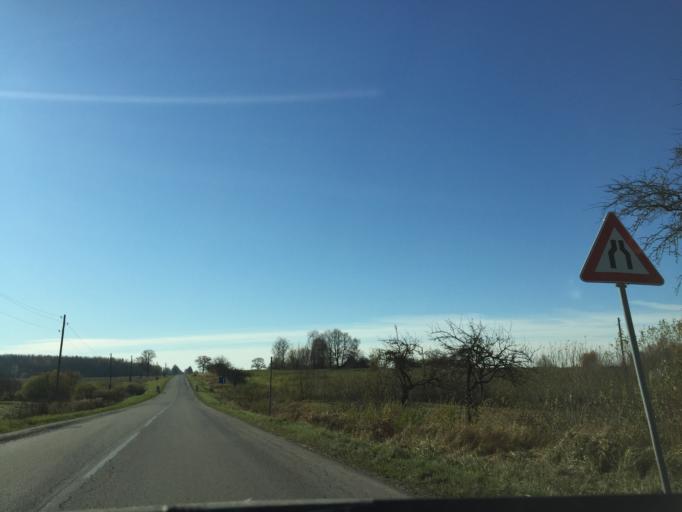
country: LV
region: Skriveri
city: Skriveri
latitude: 56.7022
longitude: 25.1519
